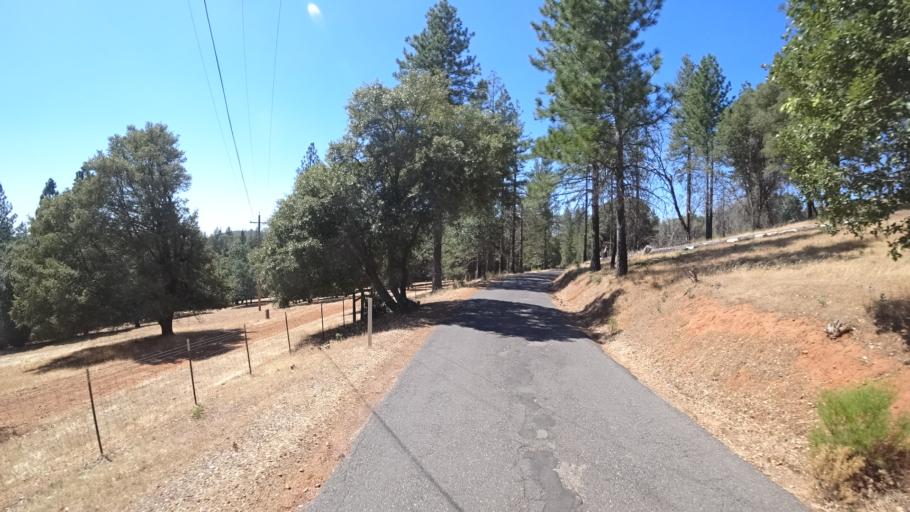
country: US
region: California
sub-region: Calaveras County
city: Mountain Ranch
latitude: 38.2888
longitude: -120.5918
